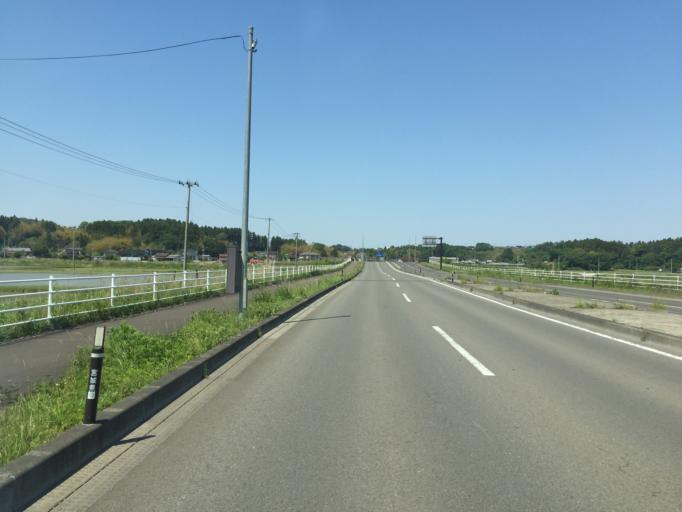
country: JP
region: Miyagi
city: Iwanuma
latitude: 38.1461
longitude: 140.8623
